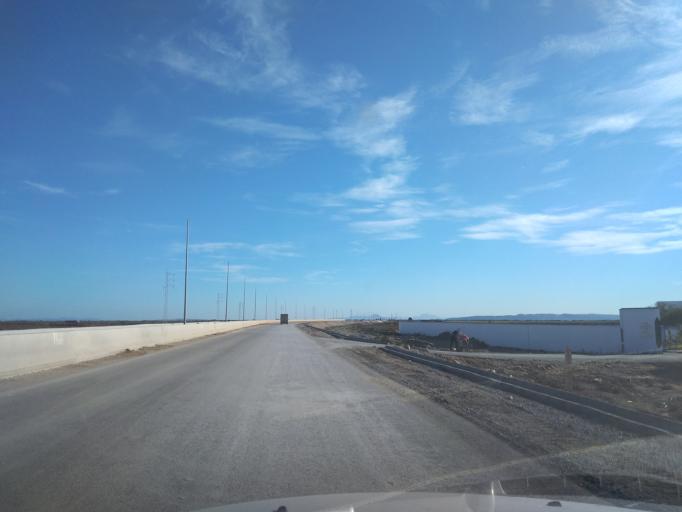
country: TN
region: Ariana
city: Qal'at al Andalus
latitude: 37.0408
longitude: 10.1306
